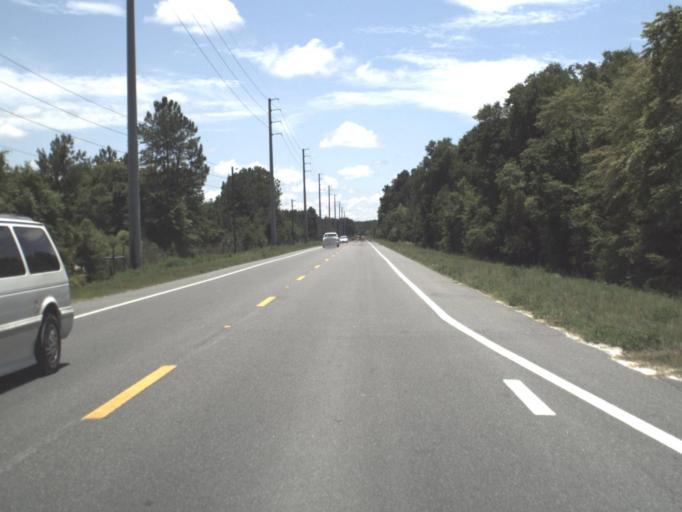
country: US
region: Florida
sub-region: Levy County
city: Manatee Road
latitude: 29.6212
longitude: -82.9832
